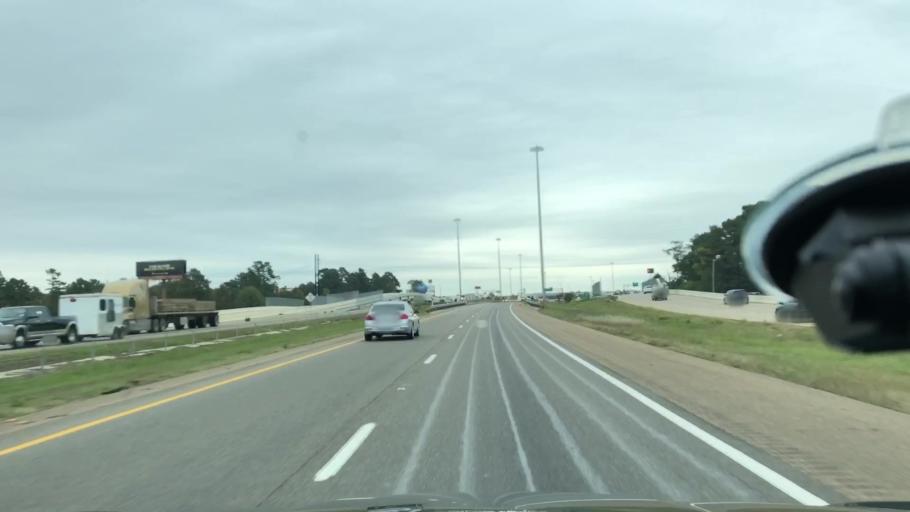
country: US
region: Arkansas
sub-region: Miller County
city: Texarkana
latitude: 33.4698
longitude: -94.0529
